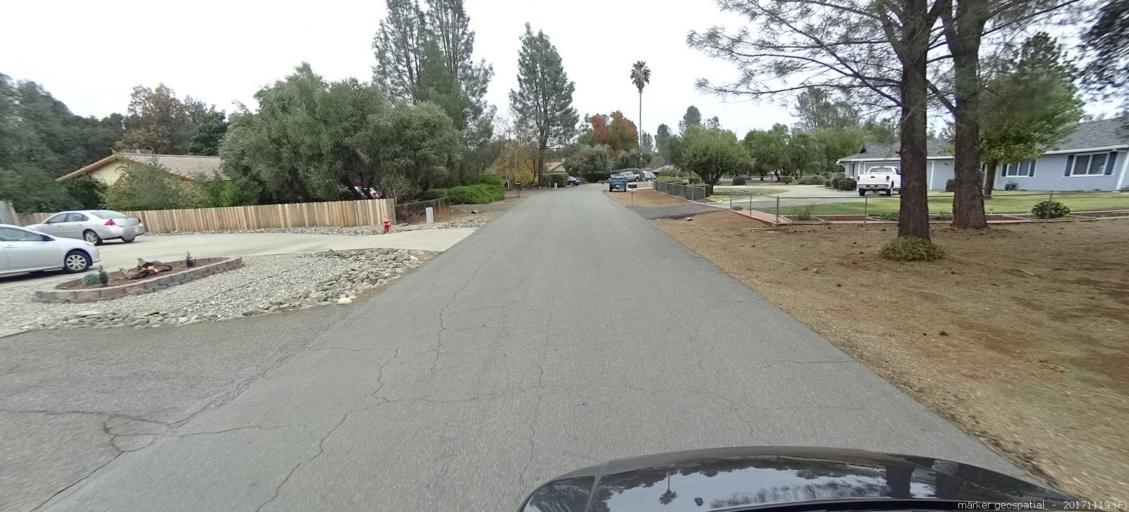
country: US
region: California
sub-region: Shasta County
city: Redding
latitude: 40.4887
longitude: -122.4168
